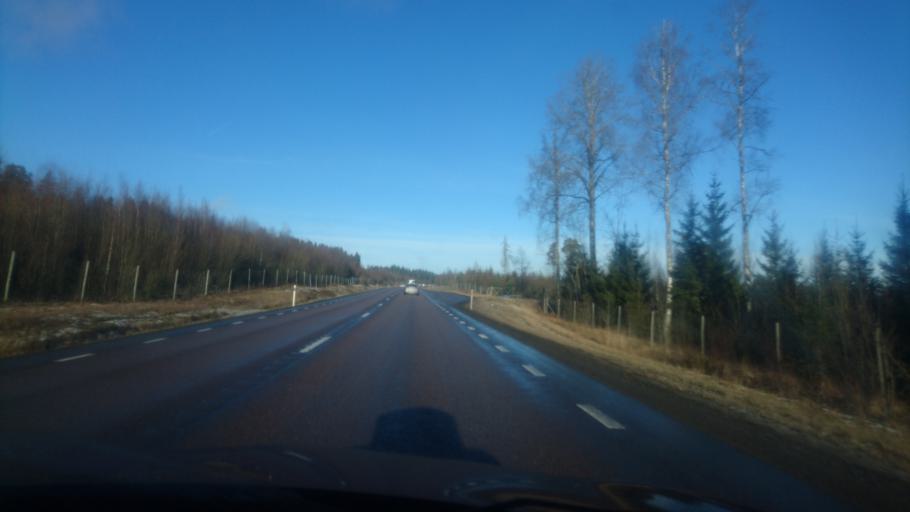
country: SE
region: Vaermland
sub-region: Sunne Kommun
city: Sunne
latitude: 59.7447
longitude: 13.1268
